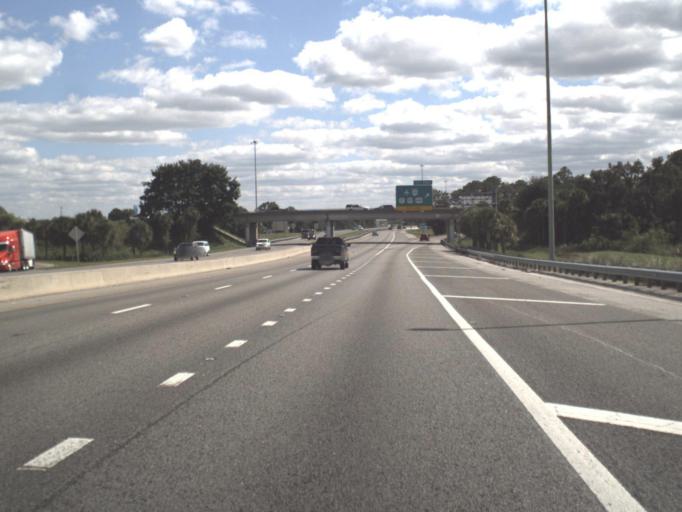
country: US
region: Florida
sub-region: Orange County
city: Sky Lake
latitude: 28.4282
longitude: -81.4020
